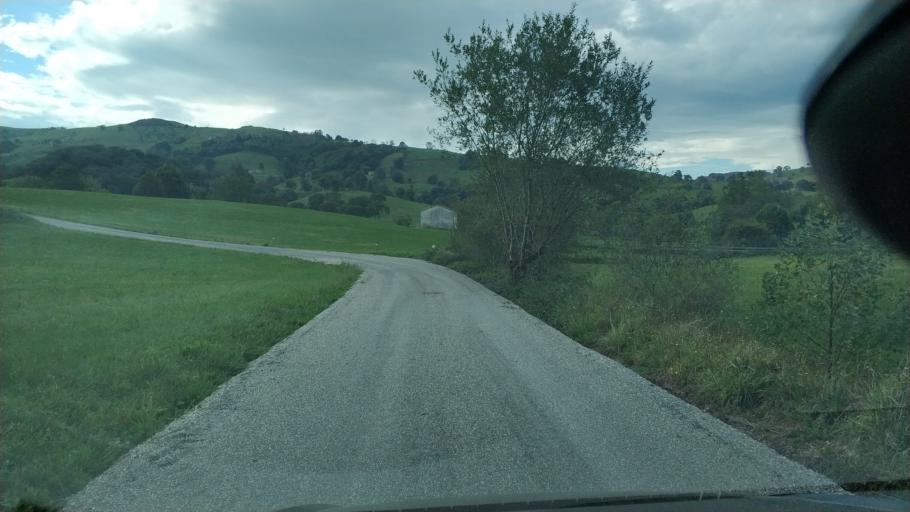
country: ES
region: Cantabria
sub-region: Provincia de Cantabria
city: Santa Maria de Cayon
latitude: 43.2847
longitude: -3.8128
